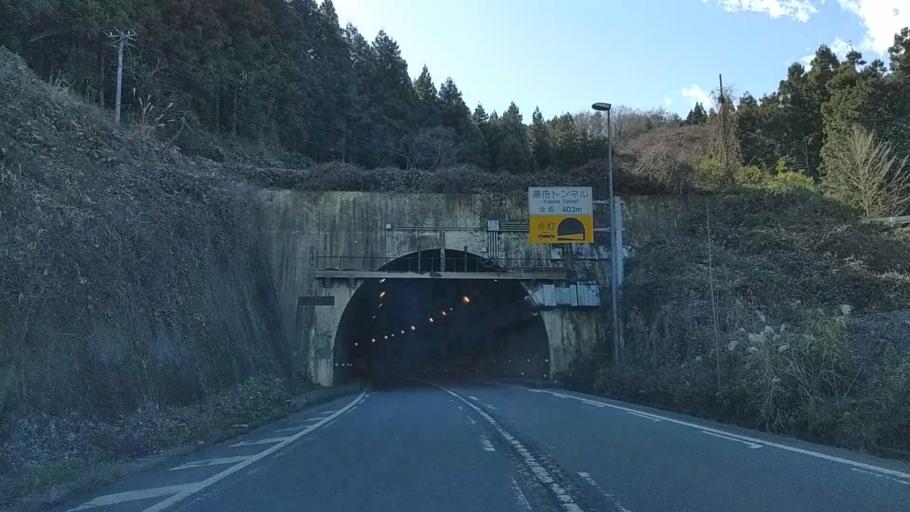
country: JP
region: Shizuoka
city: Gotemba
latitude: 35.3662
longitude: 138.9774
